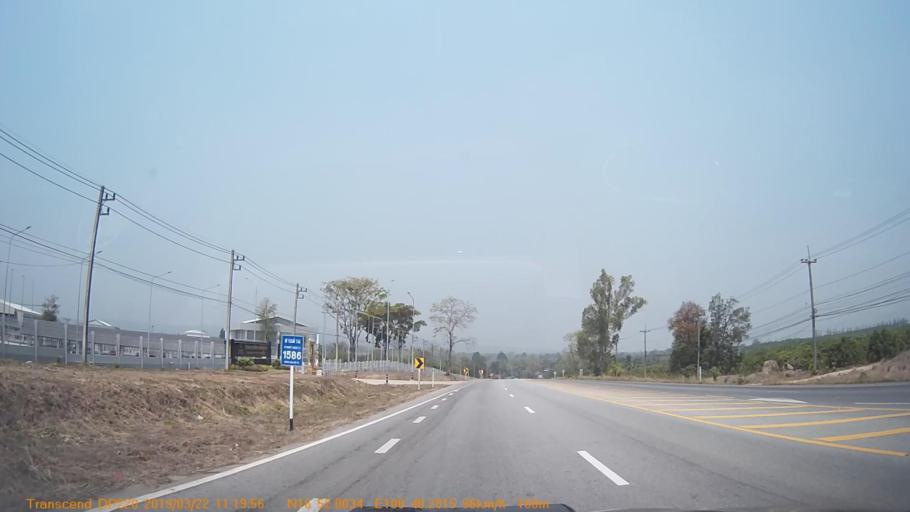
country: TH
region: Phitsanulok
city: Wang Thong
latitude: 16.8669
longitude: 100.6711
